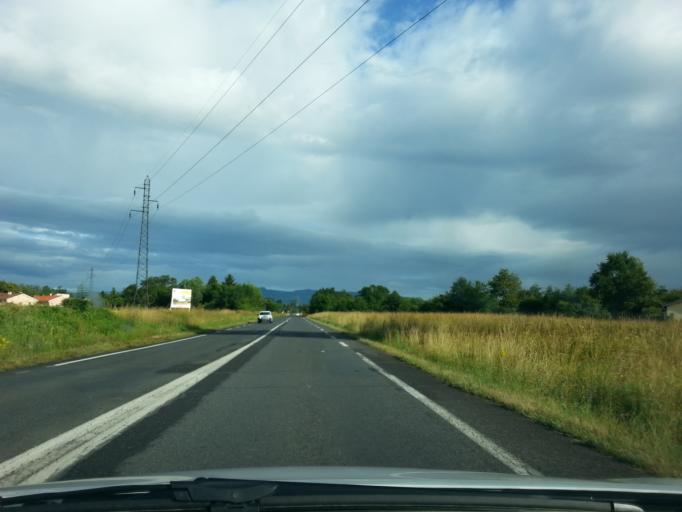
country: FR
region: Rhone-Alpes
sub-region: Departement du Rhone
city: Belleville
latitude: 46.1149
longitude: 4.7512
